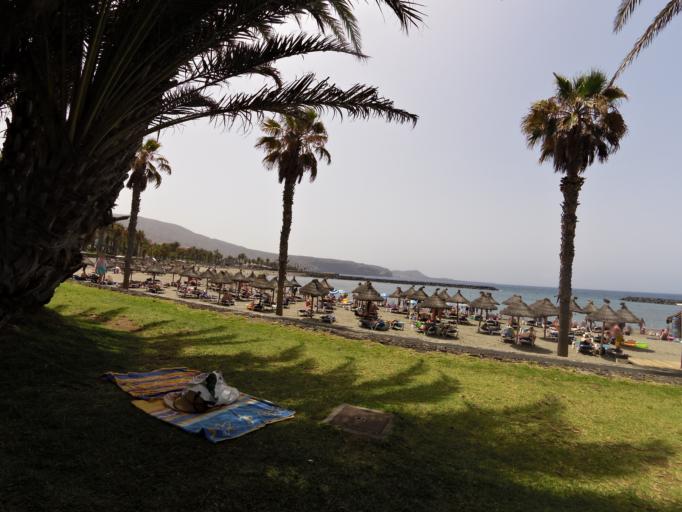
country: ES
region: Canary Islands
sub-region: Provincia de Santa Cruz de Tenerife
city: Playa de las Americas
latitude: 28.0534
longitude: -16.7330
